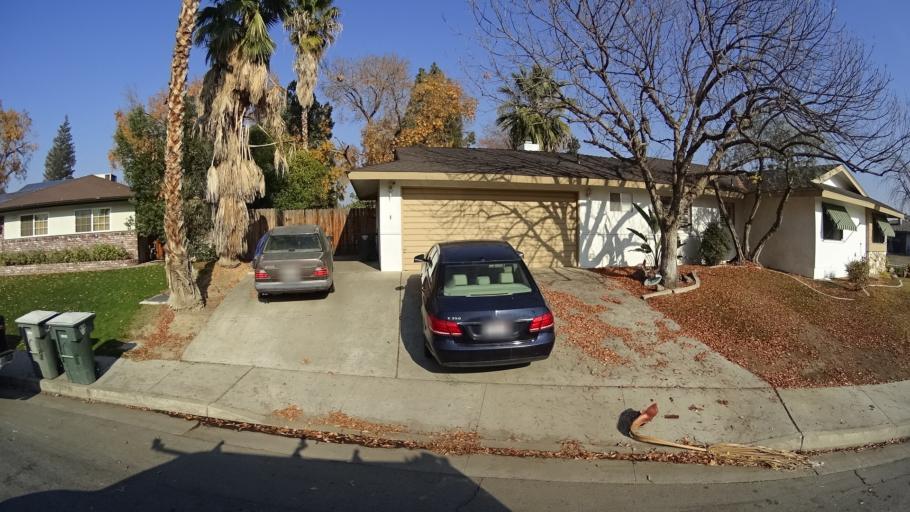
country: US
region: California
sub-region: Kern County
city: Bakersfield
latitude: 35.3627
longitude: -119.0541
